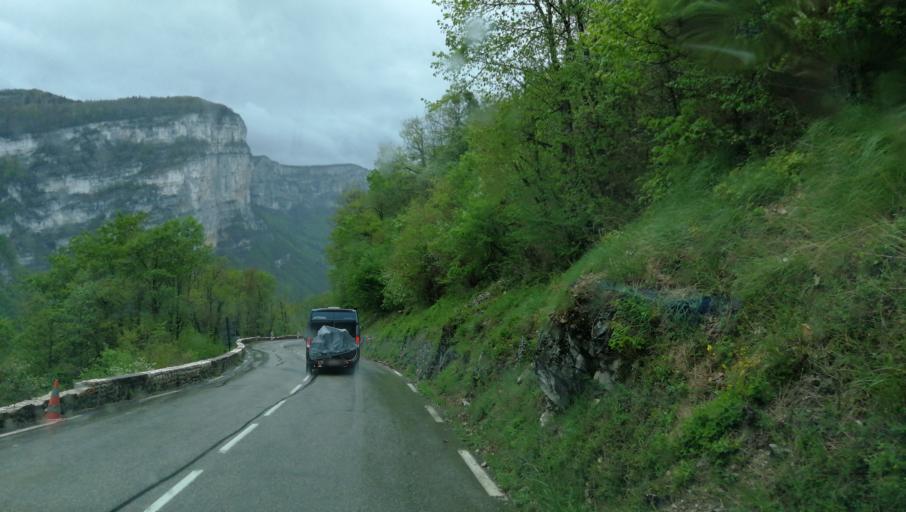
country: FR
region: Rhone-Alpes
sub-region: Departement de l'Isere
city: Pont-en-Royans
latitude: 45.0708
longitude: 5.4408
